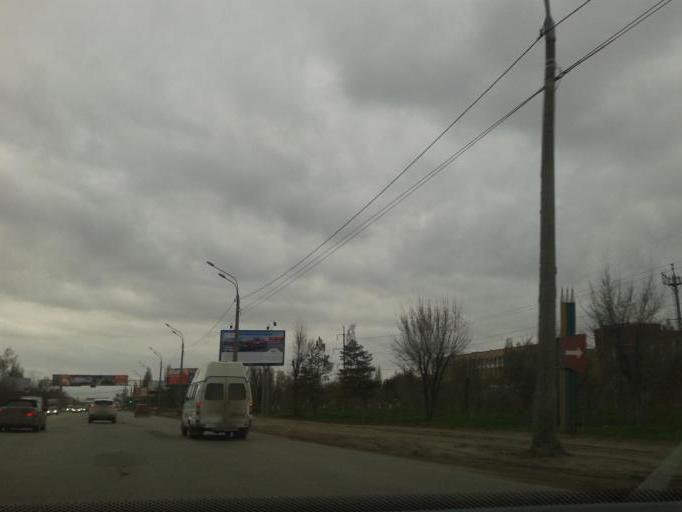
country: RU
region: Volgograd
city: Gorodishche
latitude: 48.7638
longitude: 44.4756
